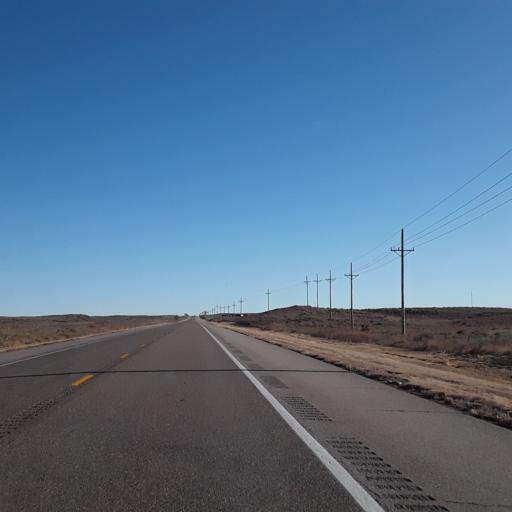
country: US
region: Kansas
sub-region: Meade County
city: Meade
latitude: 37.3896
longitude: -100.1631
